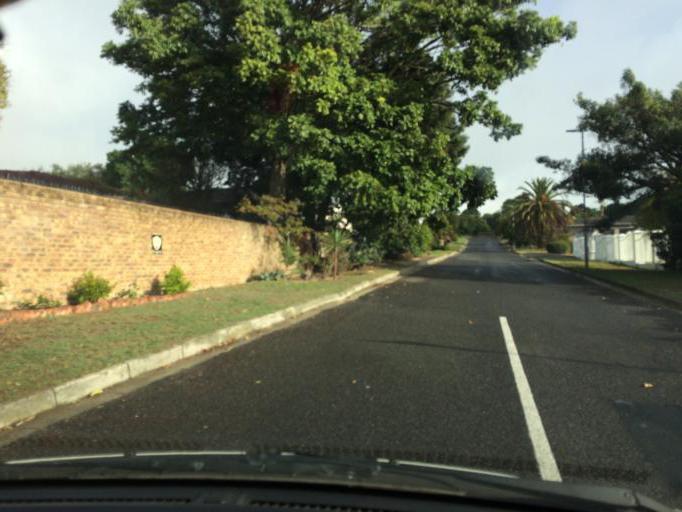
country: ZA
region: Western Cape
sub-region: City of Cape Town
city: Kraaifontein
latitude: -33.8666
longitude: 18.6503
